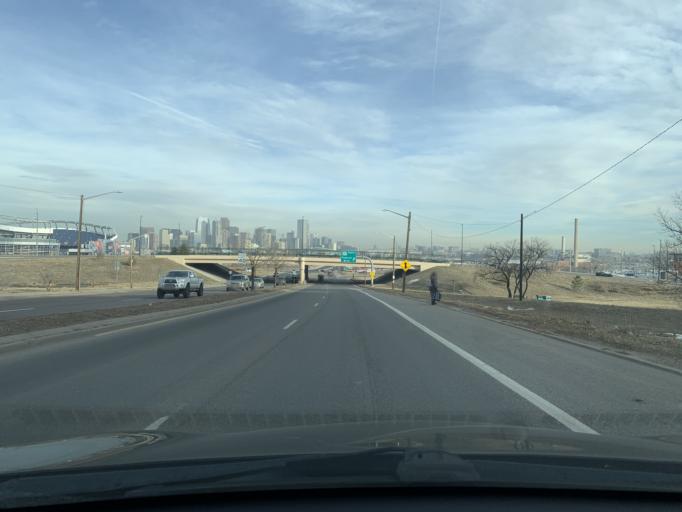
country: US
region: Colorado
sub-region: Jefferson County
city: Edgewater
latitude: 39.7403
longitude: -105.0271
